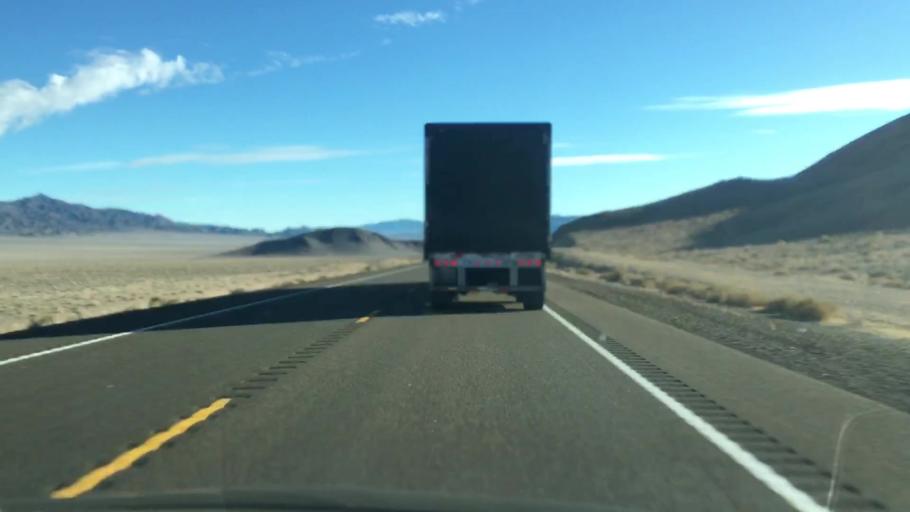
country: US
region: Nevada
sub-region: Nye County
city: Tonopah
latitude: 38.1667
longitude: -117.9546
